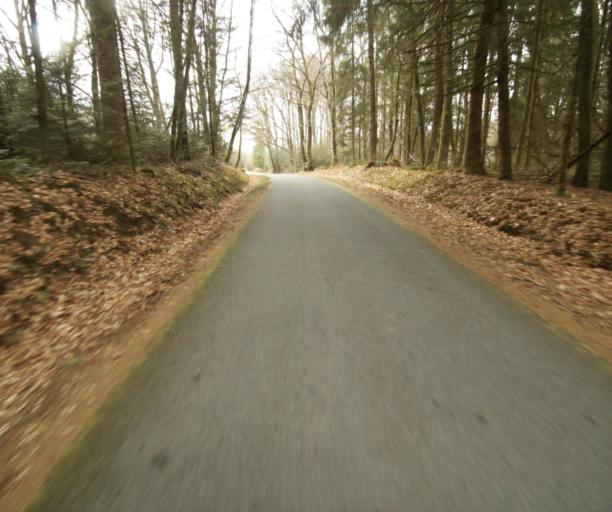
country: FR
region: Limousin
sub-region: Departement de la Correze
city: Argentat
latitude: 45.1937
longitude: 1.9165
